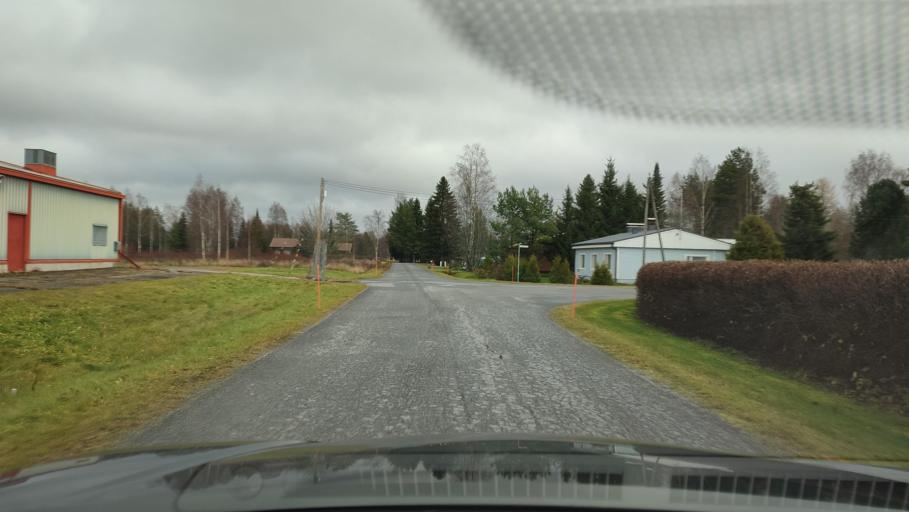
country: FI
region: Southern Ostrobothnia
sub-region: Suupohja
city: Kauhajoki
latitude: 62.4168
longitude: 22.1751
